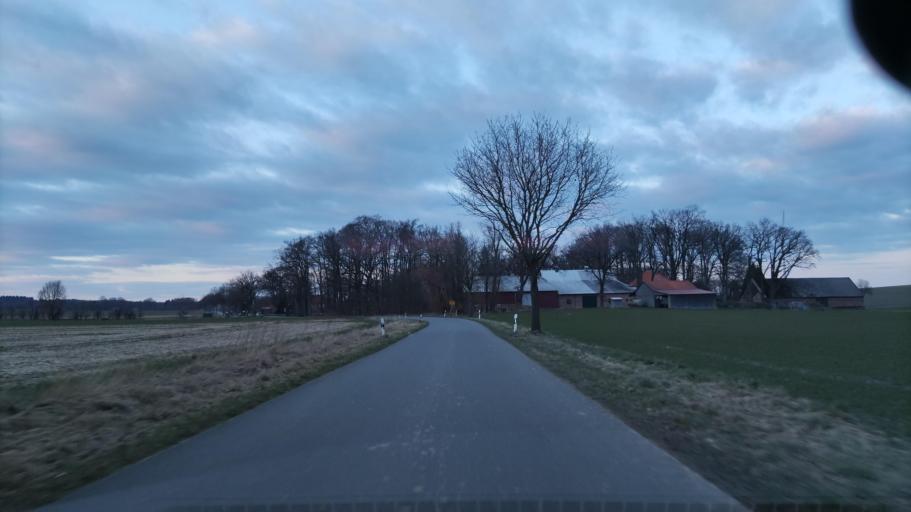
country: DE
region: Lower Saxony
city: Natendorf
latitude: 53.0821
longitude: 10.4452
